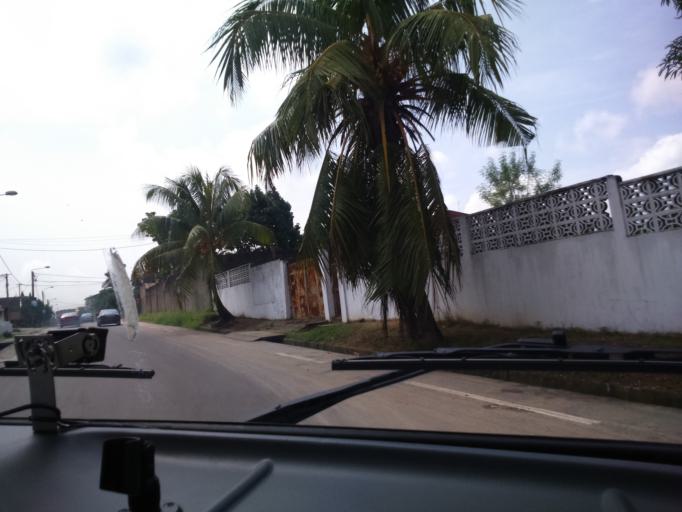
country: CI
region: Lagunes
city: Abidjan
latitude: 5.3555
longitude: -3.9810
